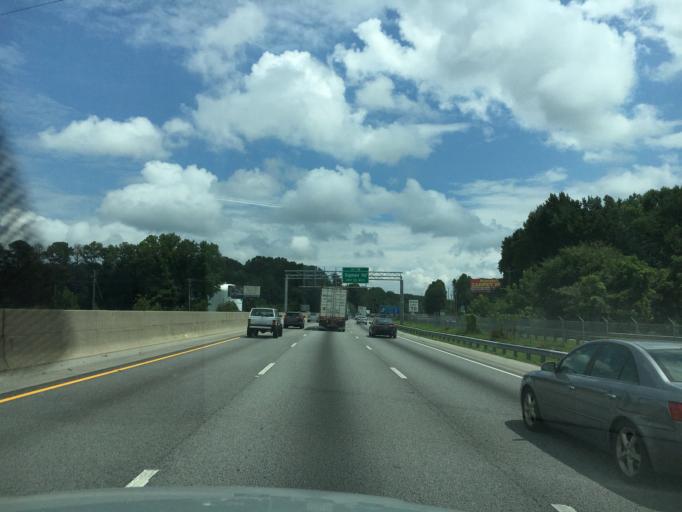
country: US
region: Georgia
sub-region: DeKalb County
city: Lithonia
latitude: 33.6915
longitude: -84.0720
